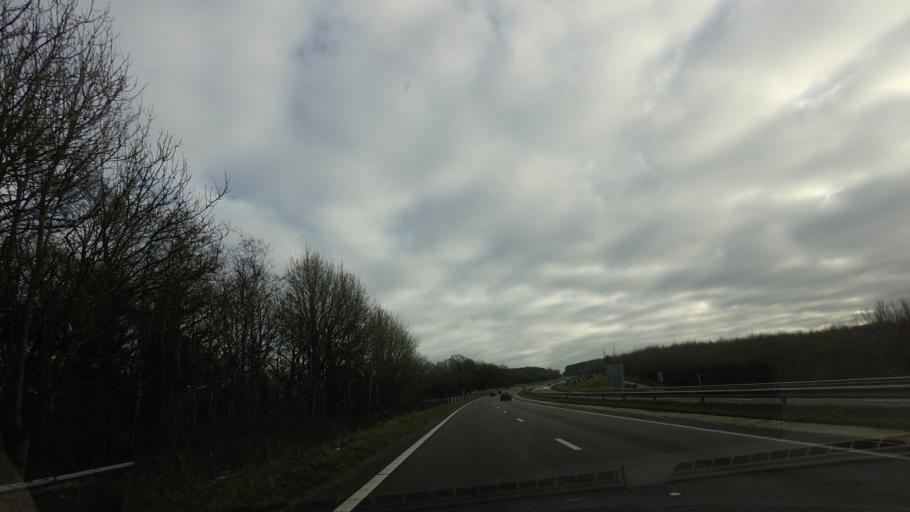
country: GB
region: England
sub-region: Kent
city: Tonbridge
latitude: 51.1800
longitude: 0.2856
